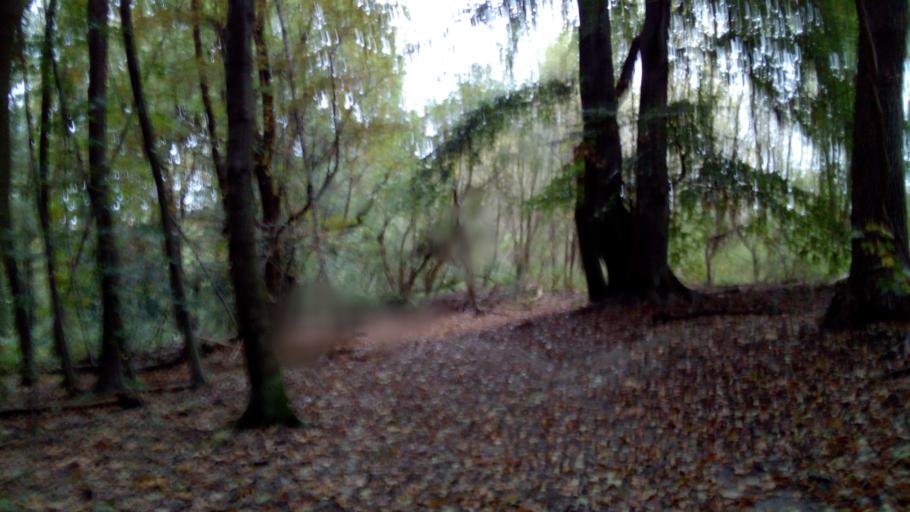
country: DE
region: North Rhine-Westphalia
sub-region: Regierungsbezirk Arnsberg
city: Bochum
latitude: 51.4442
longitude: 7.2473
